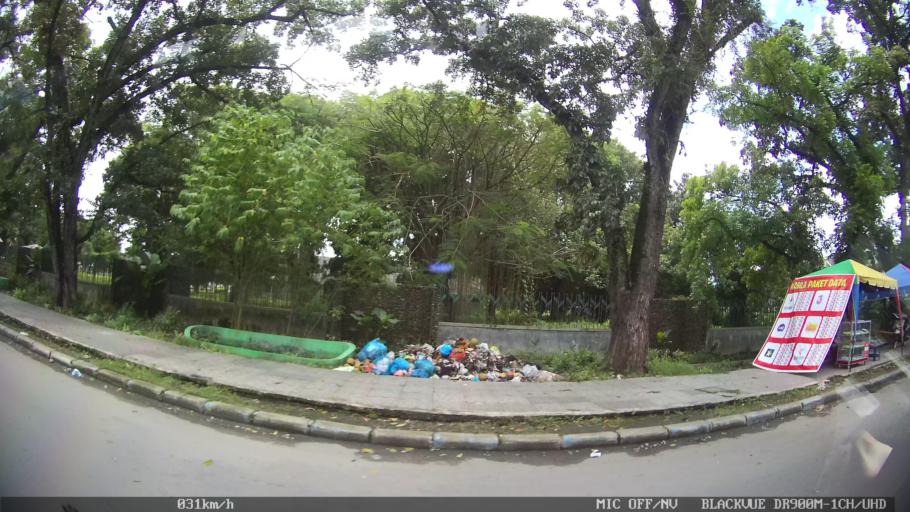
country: ID
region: North Sumatra
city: Medan
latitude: 3.6144
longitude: 98.7115
